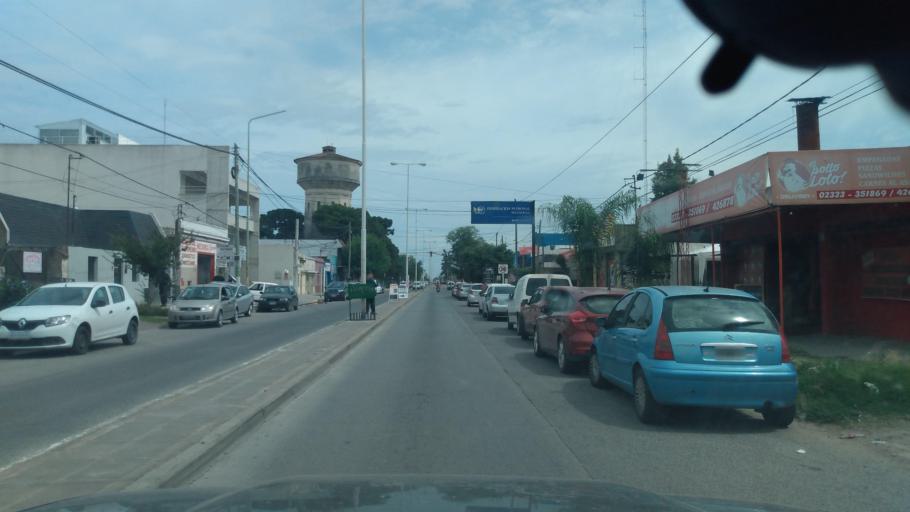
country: AR
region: Buenos Aires
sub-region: Partido de Lujan
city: Lujan
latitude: -34.5733
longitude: -59.0918
